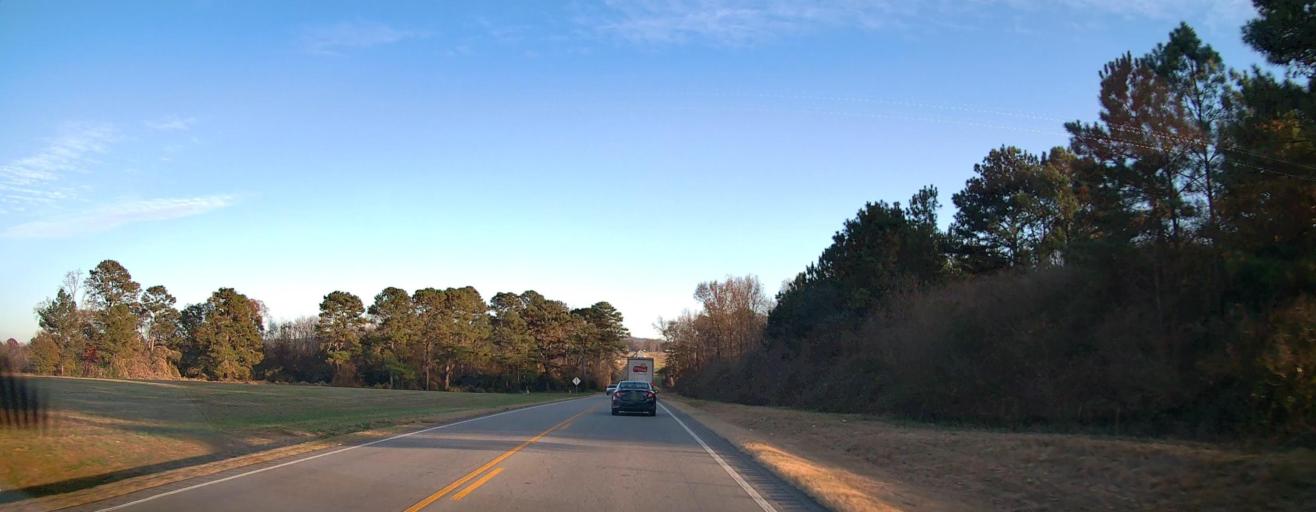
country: US
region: Alabama
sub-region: Blount County
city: Oneonta
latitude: 34.1029
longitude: -86.3693
